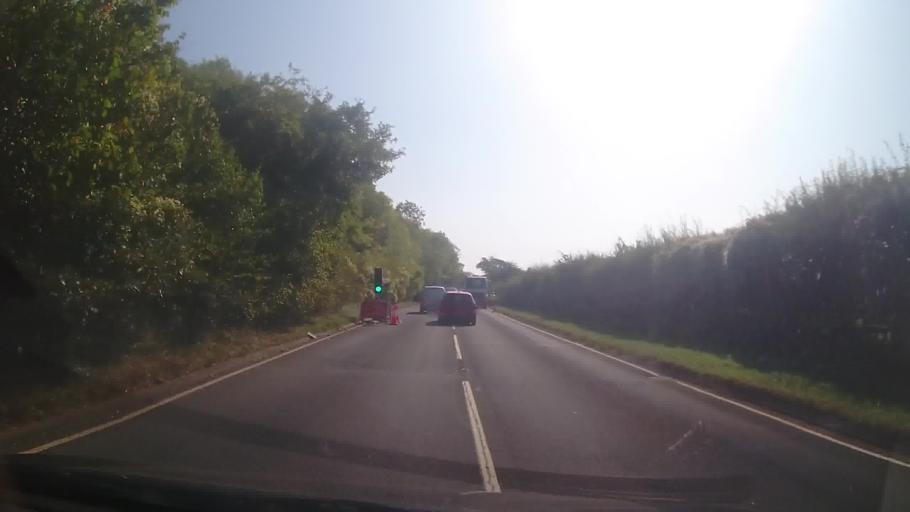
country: GB
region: England
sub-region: Worcestershire
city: Evesham
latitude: 52.1233
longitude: -1.9816
